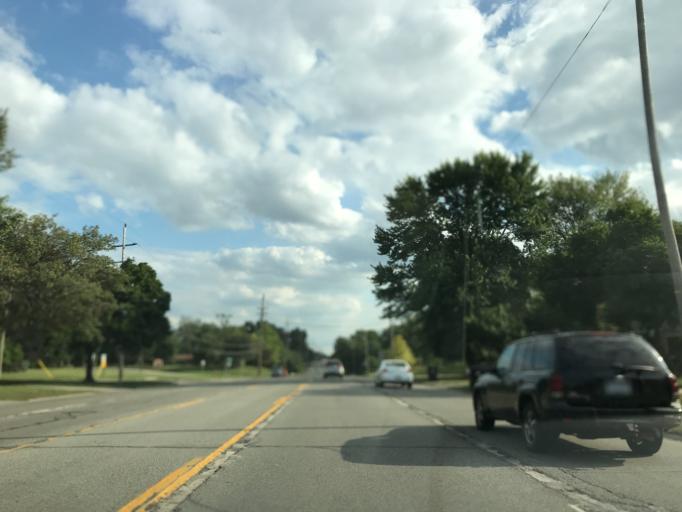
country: US
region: Michigan
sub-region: Wayne County
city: Redford
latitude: 42.4096
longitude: -83.2964
